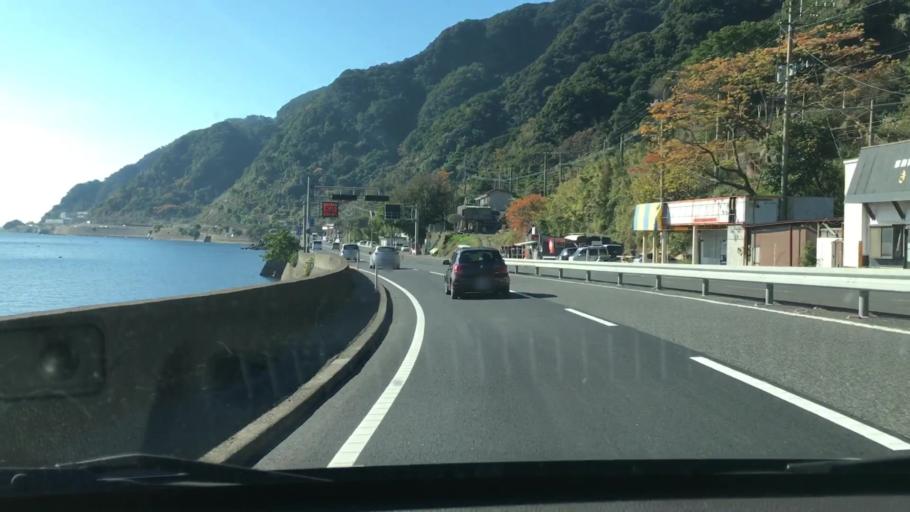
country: JP
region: Kagoshima
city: Kagoshima-shi
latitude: 31.6501
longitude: 130.6062
